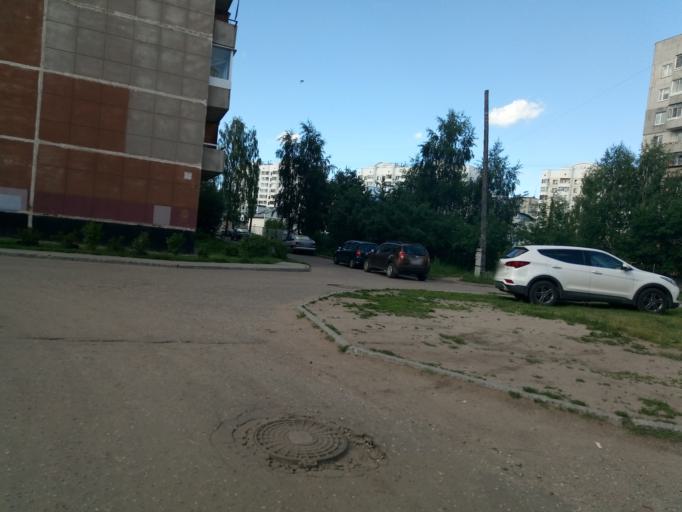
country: RU
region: Jaroslavl
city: Yaroslavl
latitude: 57.6391
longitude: 39.9503
